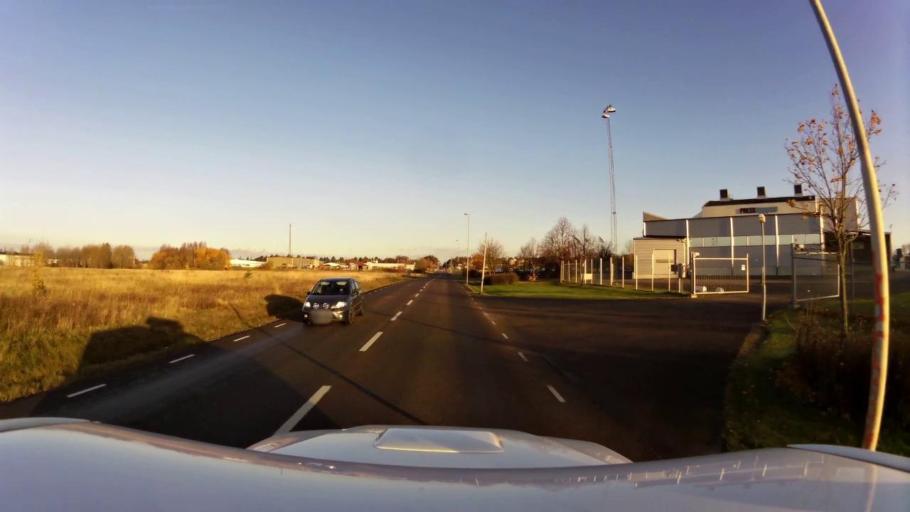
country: SE
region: OEstergoetland
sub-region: Linkopings Kommun
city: Linkoping
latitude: 58.4195
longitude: 15.6801
